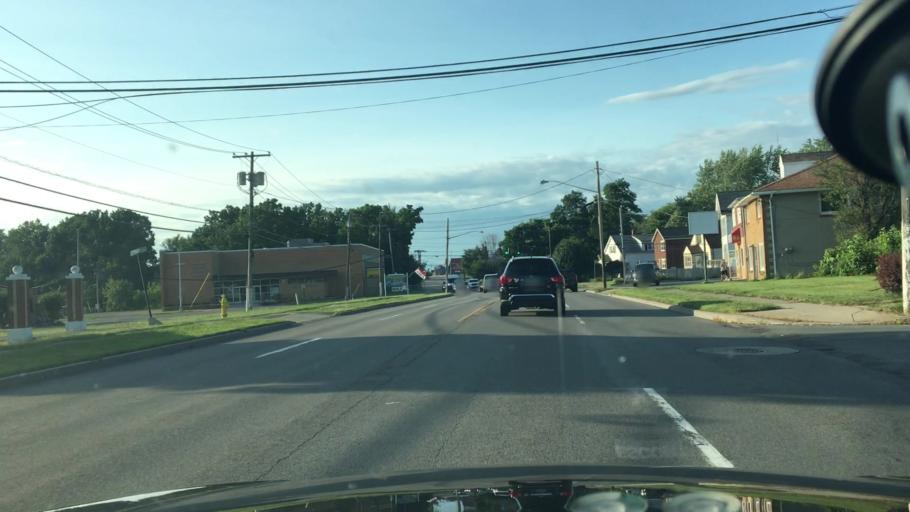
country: US
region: New York
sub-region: Erie County
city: Lackawanna
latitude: 42.8209
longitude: -78.8021
